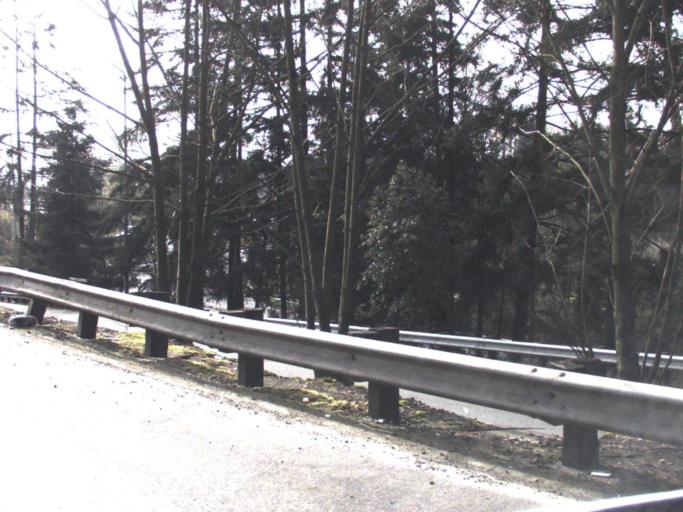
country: US
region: Washington
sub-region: King County
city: Algona
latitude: 47.3034
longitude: -122.2595
